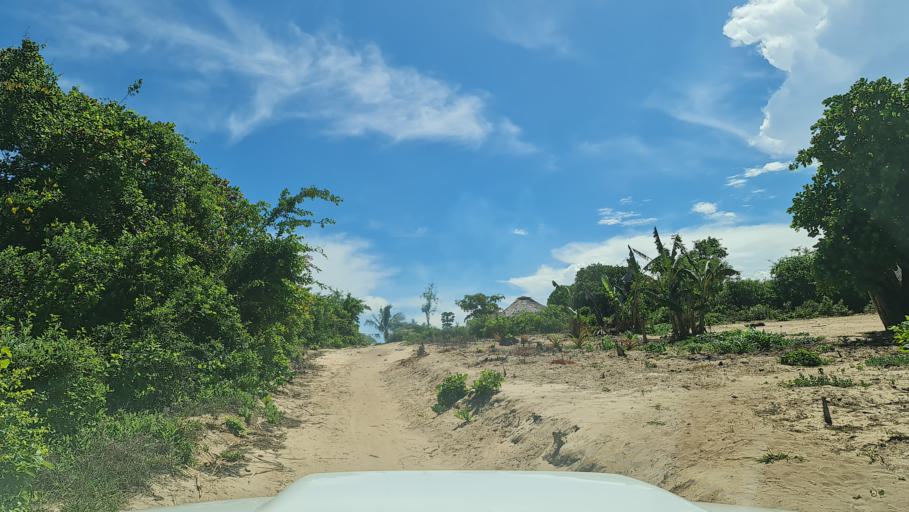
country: MZ
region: Nampula
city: Antonio Enes
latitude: -15.7047
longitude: 40.2630
